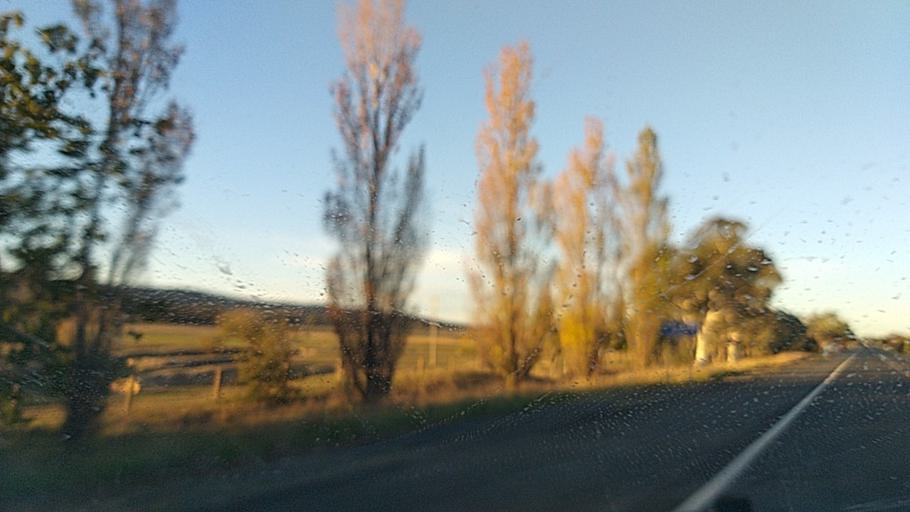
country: AU
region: New South Wales
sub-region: Goulburn Mulwaree
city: Goulburn
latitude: -34.8129
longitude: 149.6057
